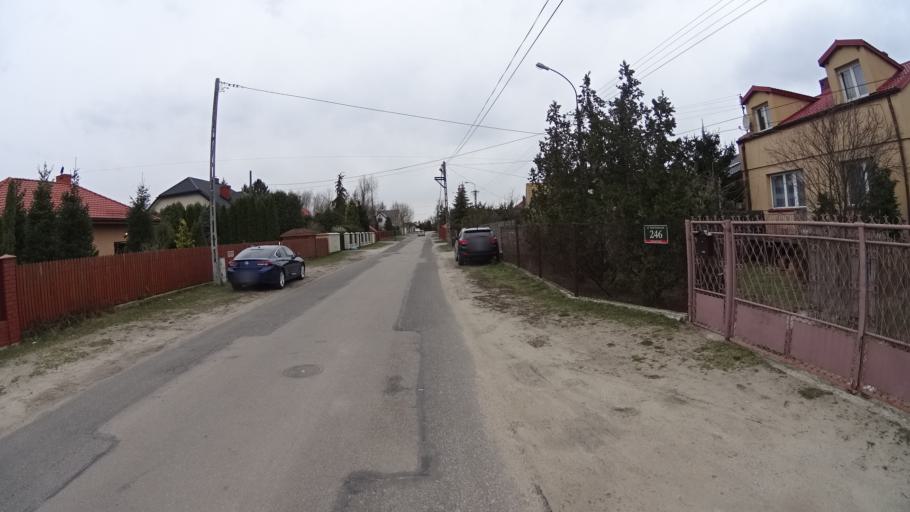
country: PL
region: Masovian Voivodeship
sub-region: Powiat warszawski zachodni
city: Truskaw
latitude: 52.2607
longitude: 20.7421
